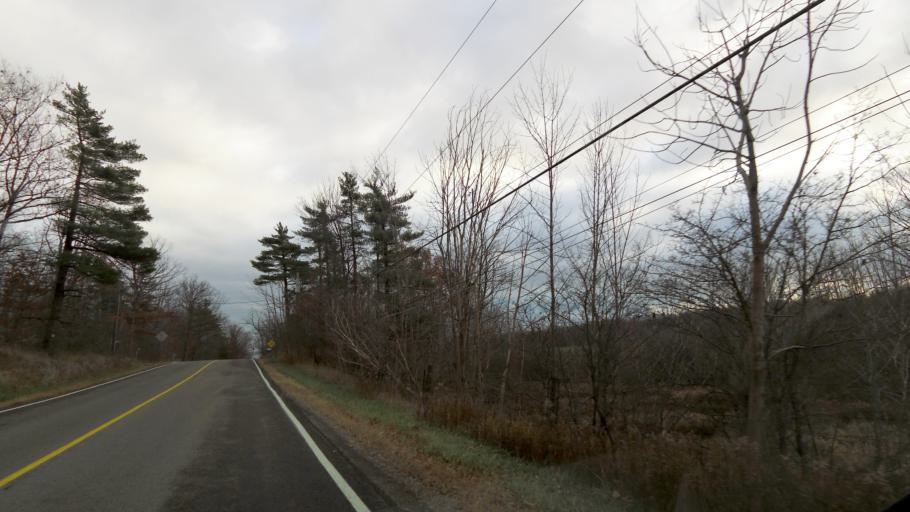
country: CA
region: Ontario
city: Burlington
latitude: 43.4044
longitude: -79.8404
